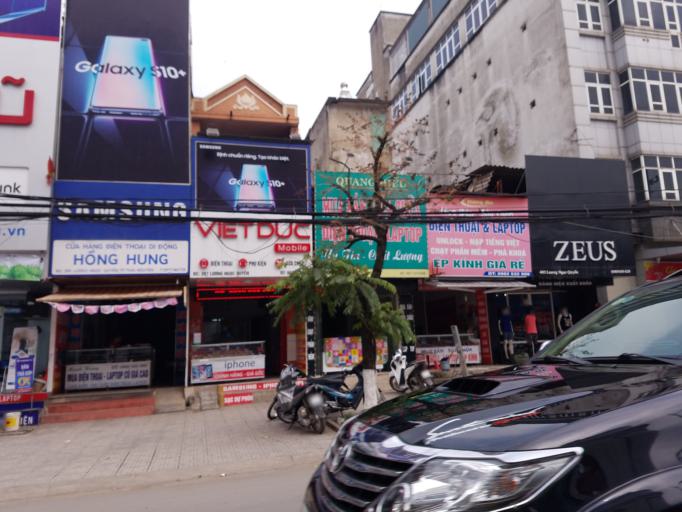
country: VN
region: Thai Nguyen
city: Thanh Pho Thai Nguyen
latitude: 21.5909
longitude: 105.8265
